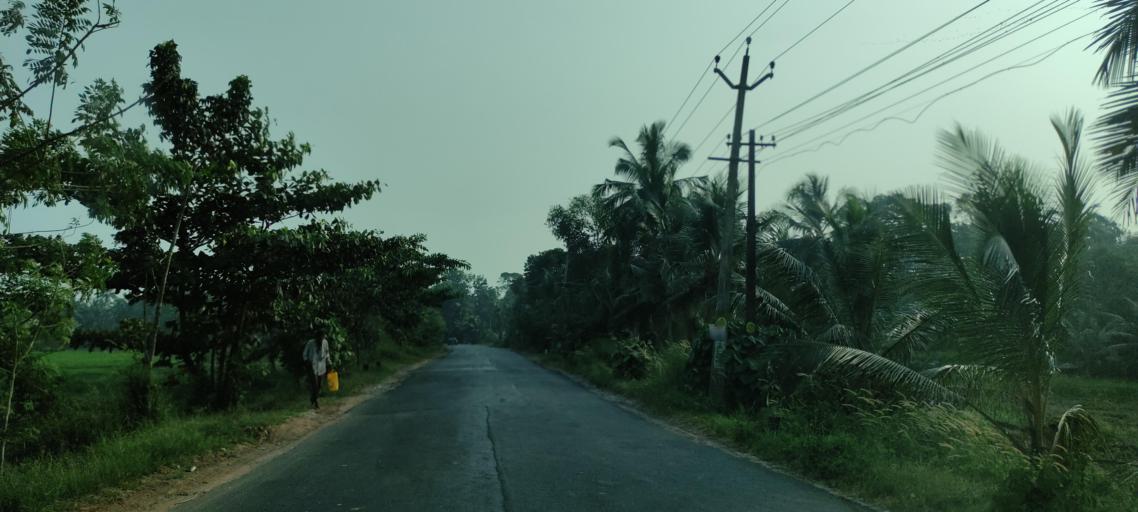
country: IN
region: Kerala
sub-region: Kottayam
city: Vaikam
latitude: 9.6913
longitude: 76.4638
